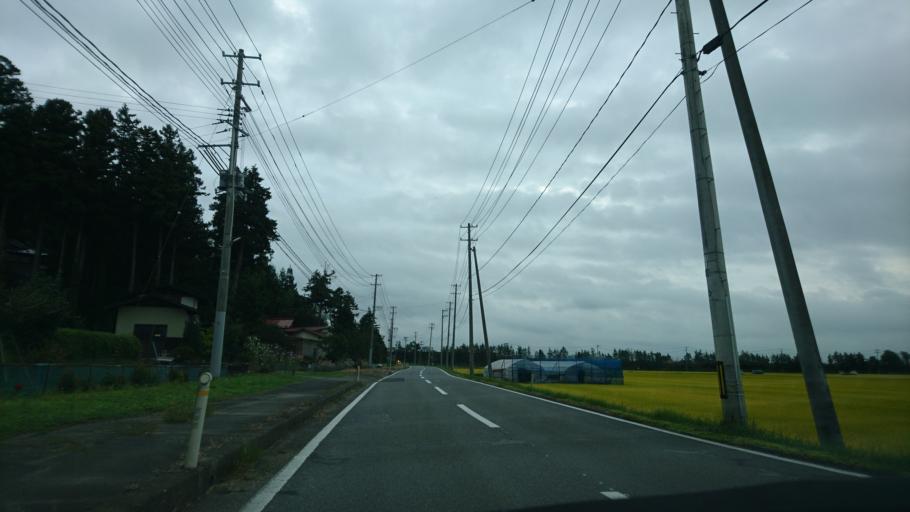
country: JP
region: Iwate
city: Ichinoseki
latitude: 38.8043
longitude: 141.0899
